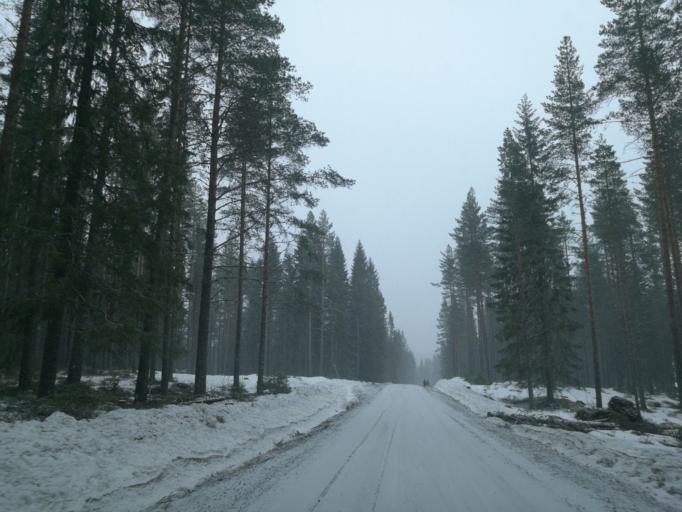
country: SE
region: Vaermland
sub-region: Torsby Kommun
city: Torsby
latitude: 60.6437
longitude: 12.7347
